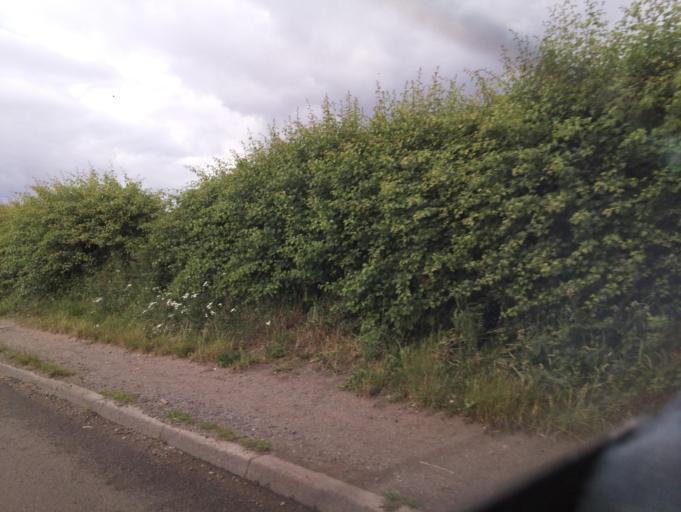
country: GB
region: England
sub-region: Dudley
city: Kingswinford
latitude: 52.5158
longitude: -2.1742
